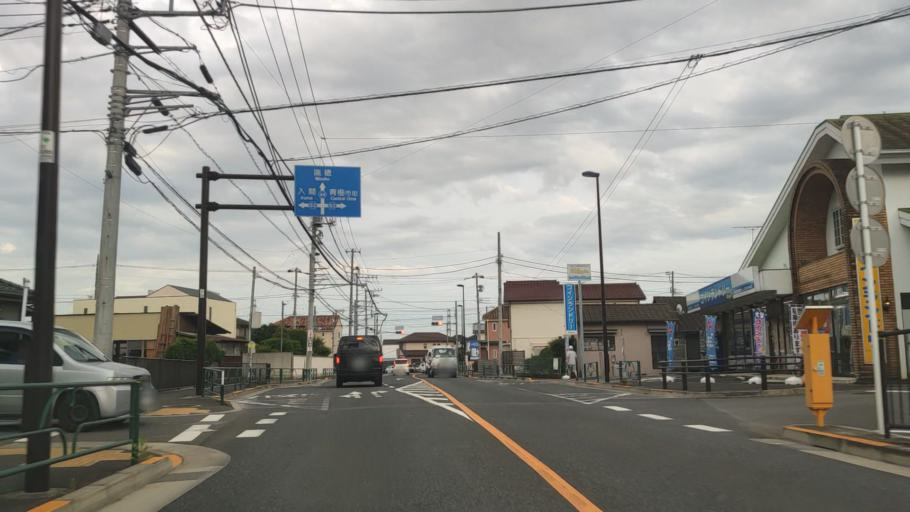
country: JP
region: Saitama
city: Hanno
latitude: 35.8049
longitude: 139.3064
